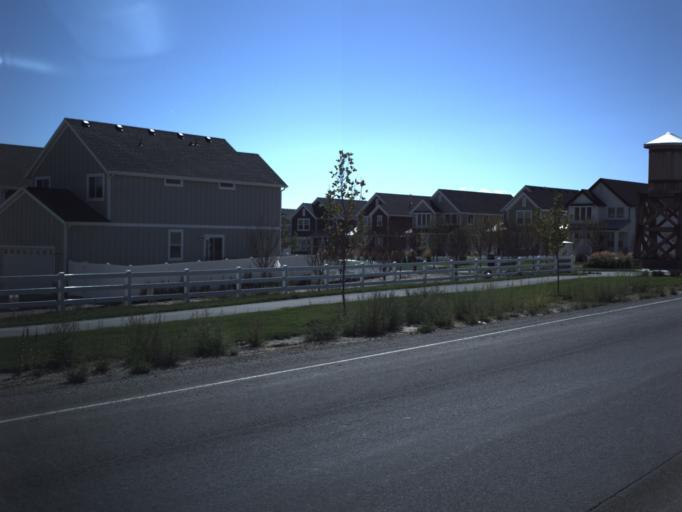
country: US
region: Utah
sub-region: Utah County
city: Saratoga Springs
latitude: 40.3530
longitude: -111.9163
